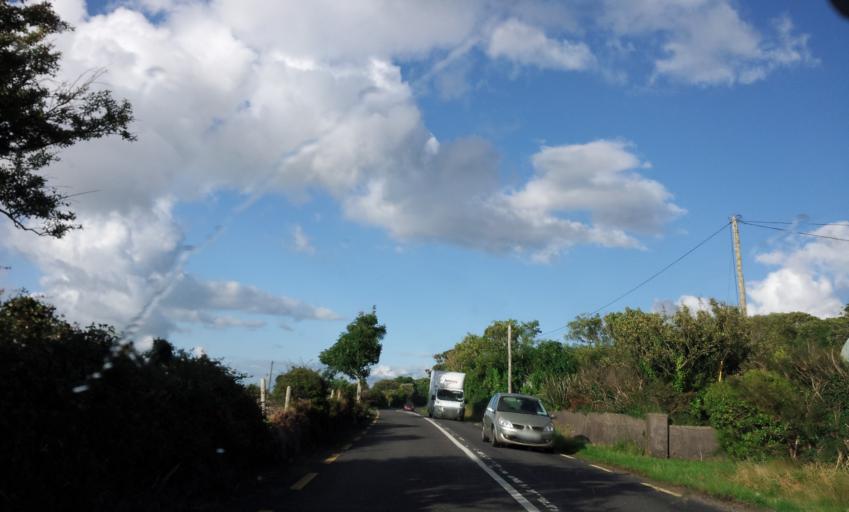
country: IE
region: Munster
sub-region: Ciarrai
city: Tralee
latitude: 52.2362
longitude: -9.8471
